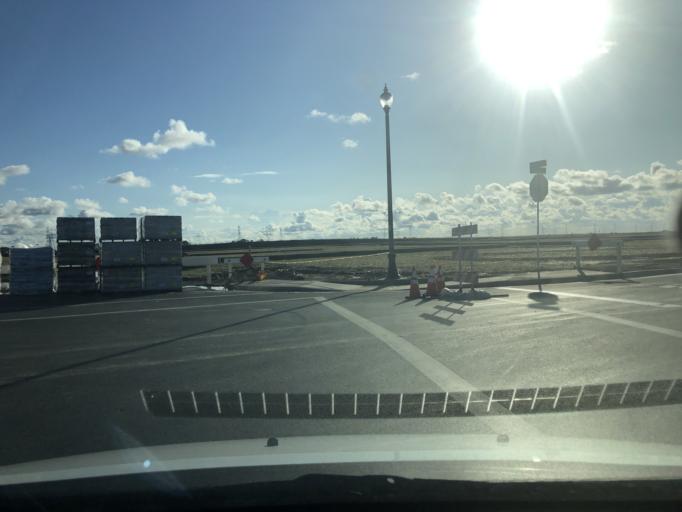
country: US
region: California
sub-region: Sacramento County
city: Elverta
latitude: 38.7710
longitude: -121.3968
